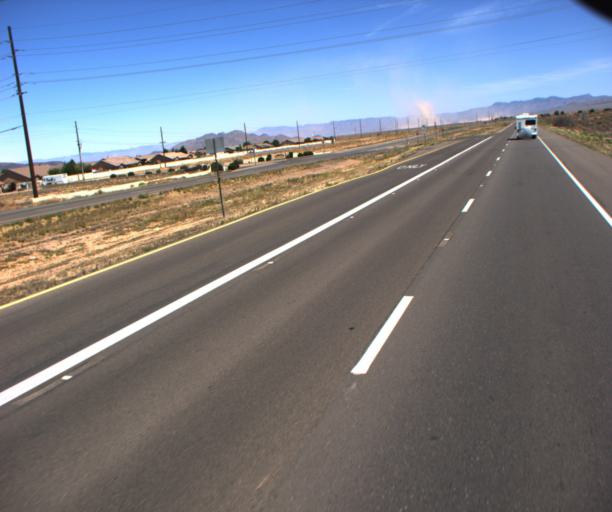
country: US
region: Arizona
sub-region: Mohave County
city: New Kingman-Butler
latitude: 35.2634
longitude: -113.9661
